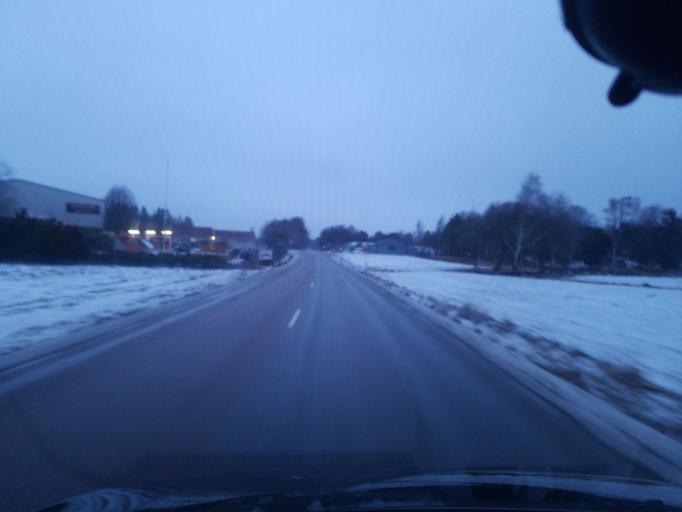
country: SE
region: Vaestra Goetaland
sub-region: Lysekils Kommun
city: Lysekil
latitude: 58.2919
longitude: 11.4773
